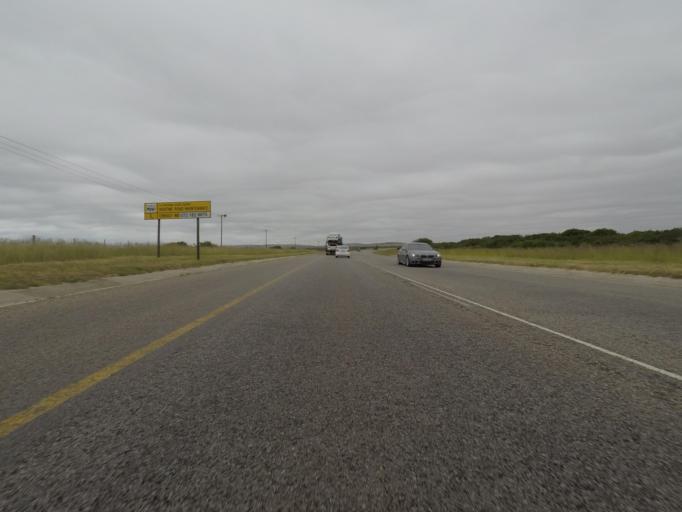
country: ZA
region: Eastern Cape
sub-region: Nelson Mandela Bay Metropolitan Municipality
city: Port Elizabeth
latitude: -33.6626
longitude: 25.8589
